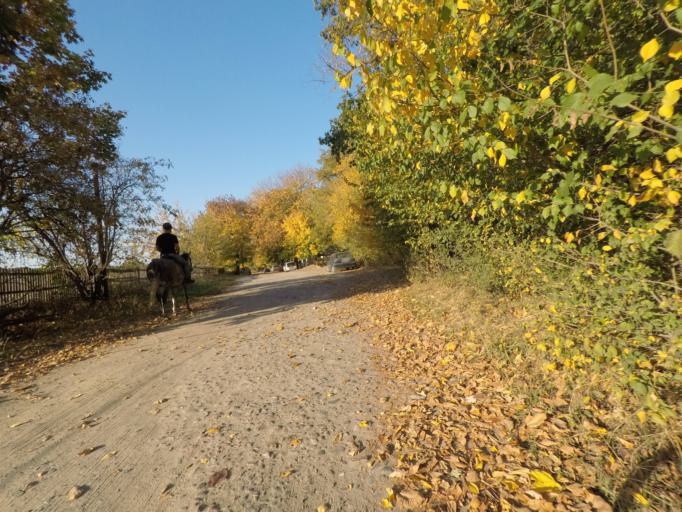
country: DE
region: Brandenburg
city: Biesenthal
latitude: 52.7764
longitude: 13.6416
